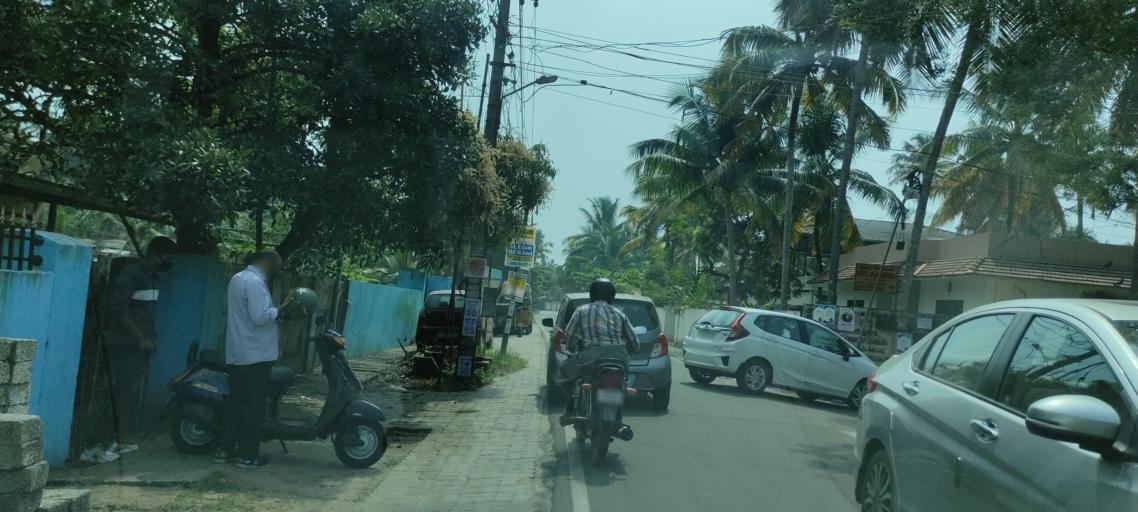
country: IN
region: Kerala
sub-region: Alappuzha
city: Alleppey
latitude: 9.5094
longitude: 76.3345
